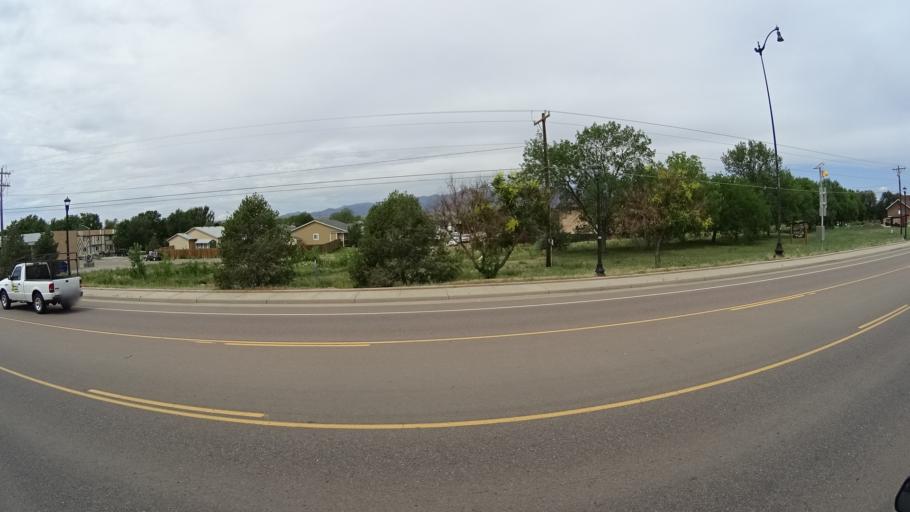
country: US
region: Colorado
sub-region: El Paso County
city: Fountain
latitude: 38.6952
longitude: -104.7051
